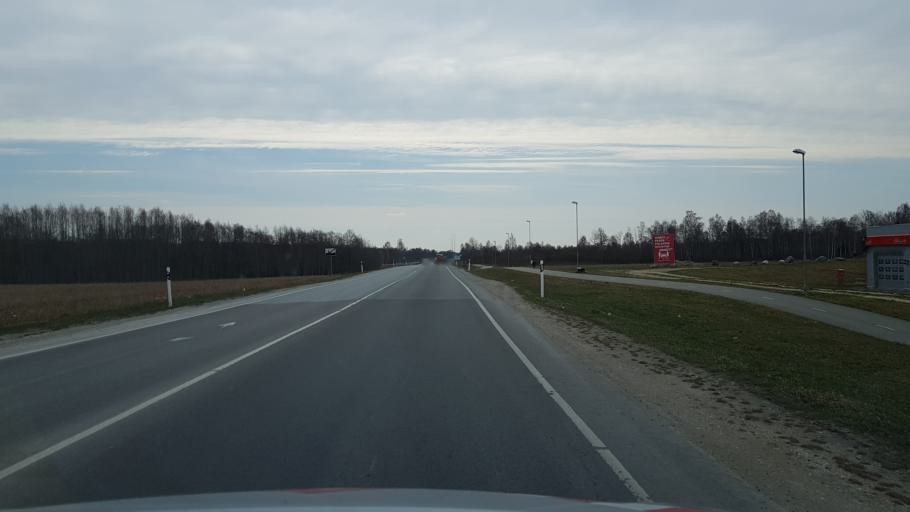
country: EE
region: Laeaene-Virumaa
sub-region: Rakvere linn
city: Rakvere
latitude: 59.3487
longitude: 26.3393
